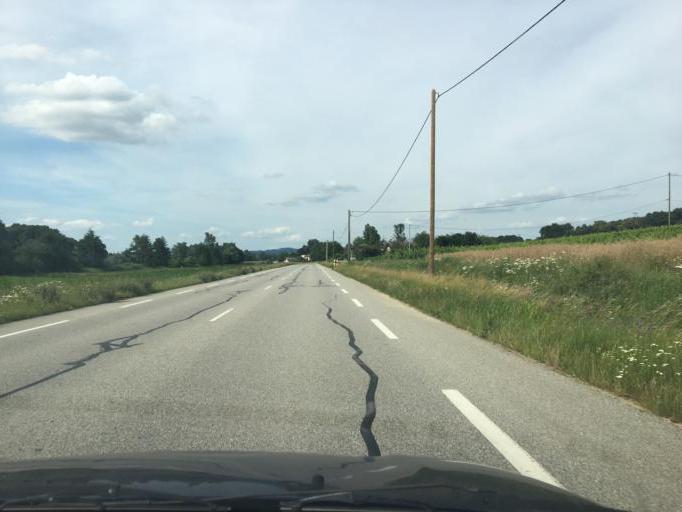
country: FR
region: Rhone-Alpes
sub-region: Departement de la Drome
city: Chanos-Curson
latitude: 45.0619
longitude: 4.9306
